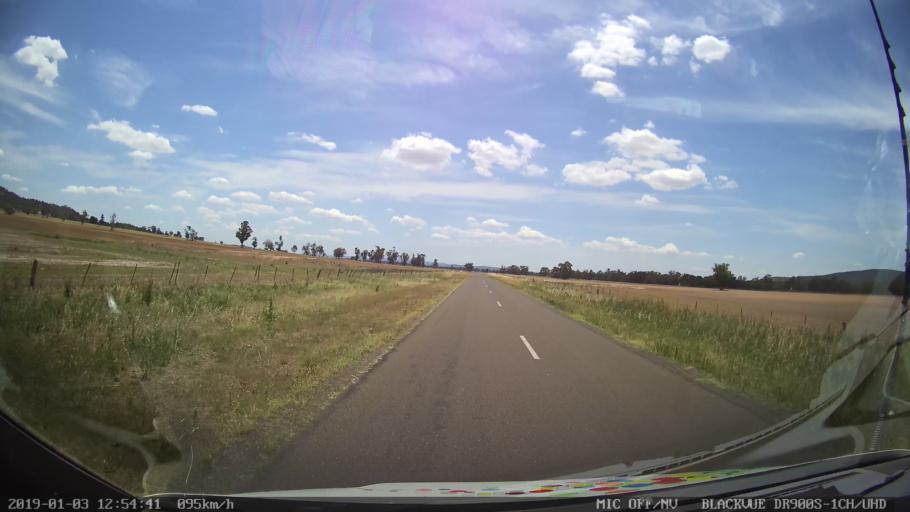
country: AU
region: New South Wales
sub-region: Weddin
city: Grenfell
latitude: -33.6502
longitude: 148.3202
